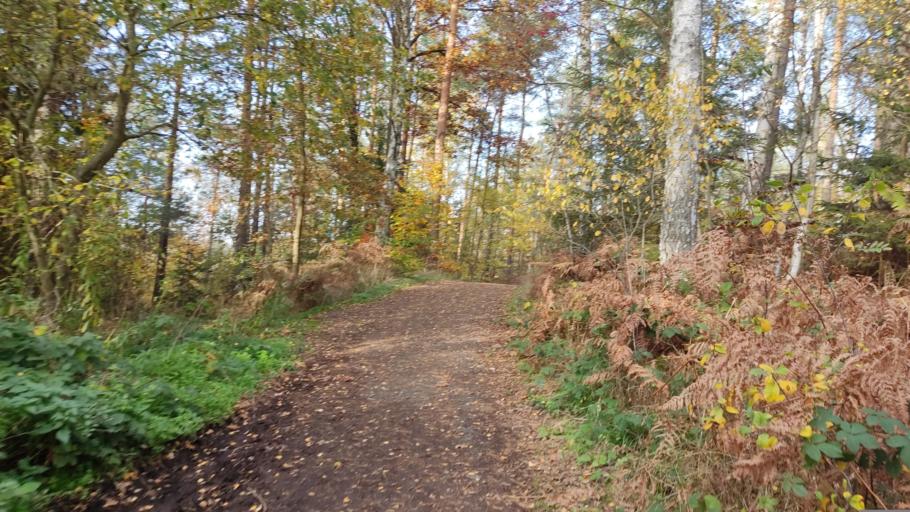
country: DE
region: Saxony
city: Struppen
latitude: 50.8977
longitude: 14.0328
